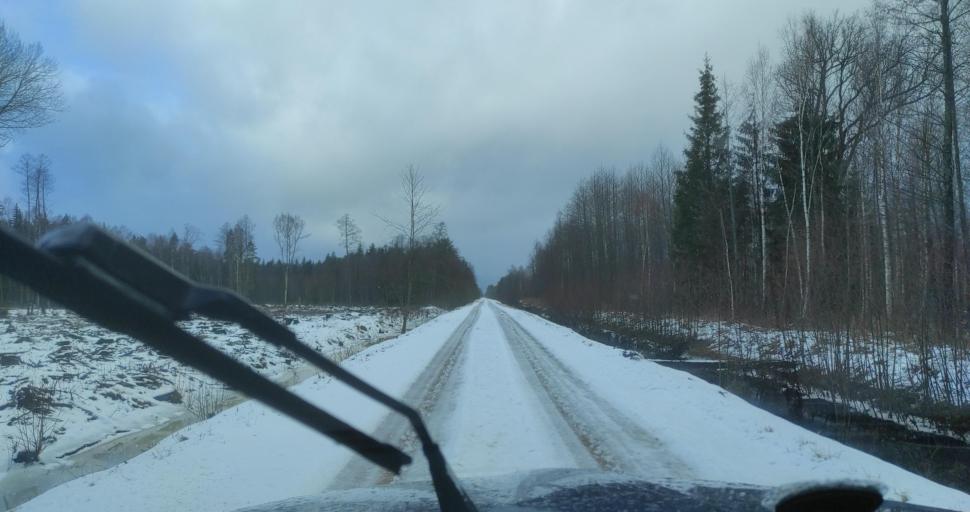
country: LV
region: Dundaga
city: Dundaga
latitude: 57.3952
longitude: 22.1206
